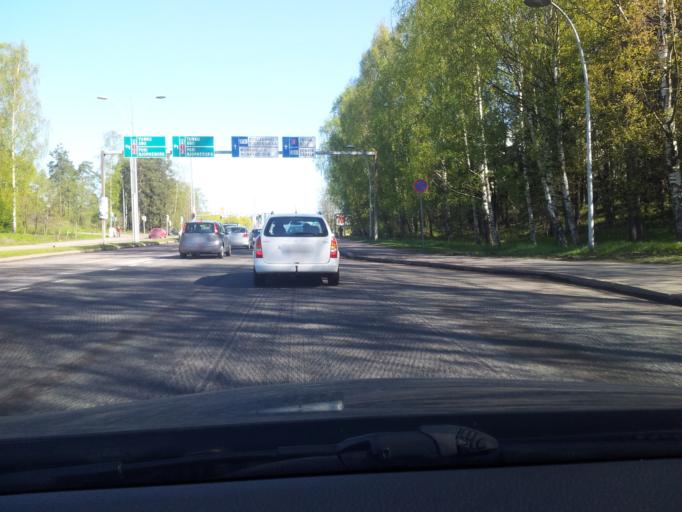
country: FI
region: Uusimaa
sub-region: Helsinki
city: Teekkarikylae
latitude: 60.2028
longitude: 24.8817
